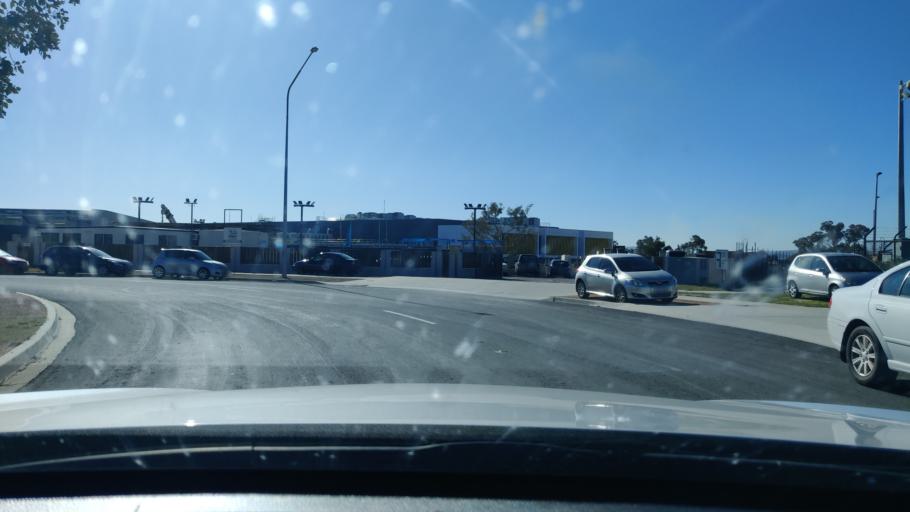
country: AU
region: Australian Capital Territory
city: Macarthur
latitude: -35.3980
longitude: 149.1638
